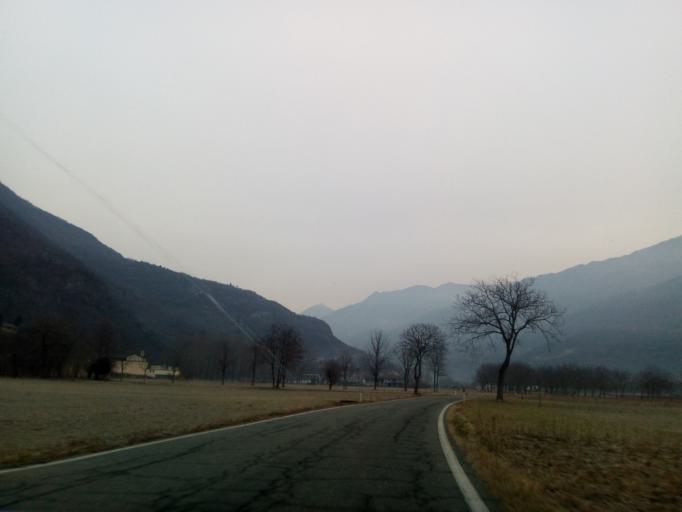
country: IT
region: Piedmont
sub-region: Provincia di Torino
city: Quassolo
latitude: 45.5133
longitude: 7.8323
